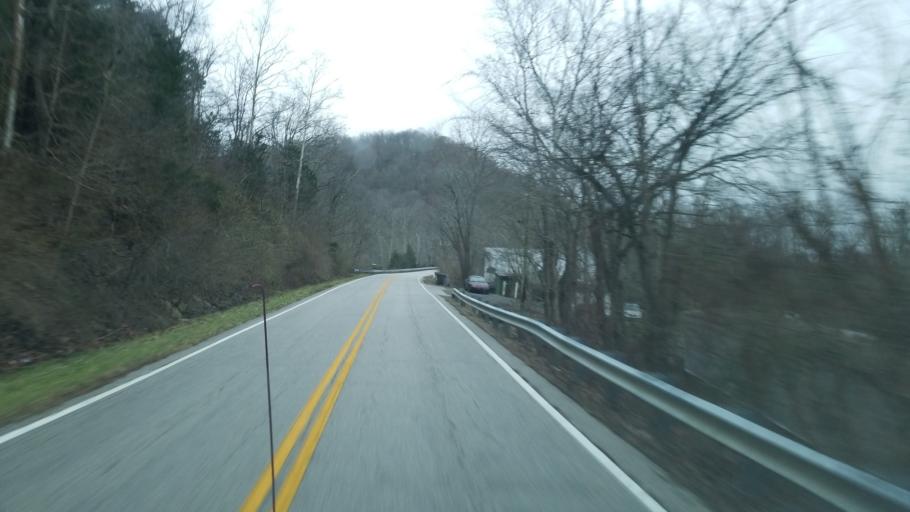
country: US
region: Kentucky
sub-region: Bracken County
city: Augusta
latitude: 38.7660
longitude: -84.0680
